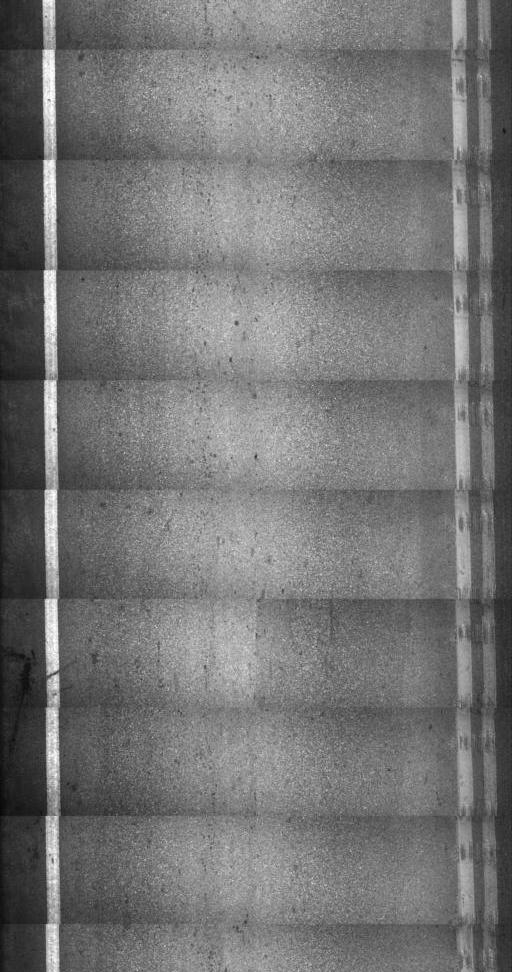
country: US
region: Vermont
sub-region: Franklin County
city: Swanton
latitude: 44.9261
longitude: -72.9751
